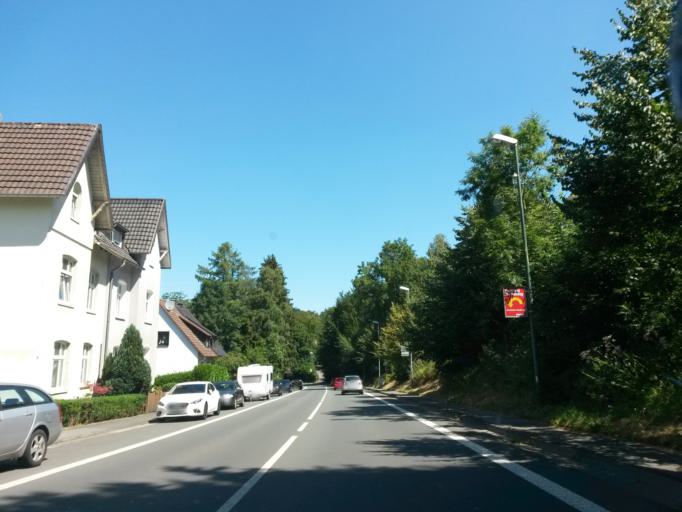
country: DE
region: North Rhine-Westphalia
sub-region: Regierungsbezirk Arnsberg
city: Luedenscheid
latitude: 51.2317
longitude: 7.6127
